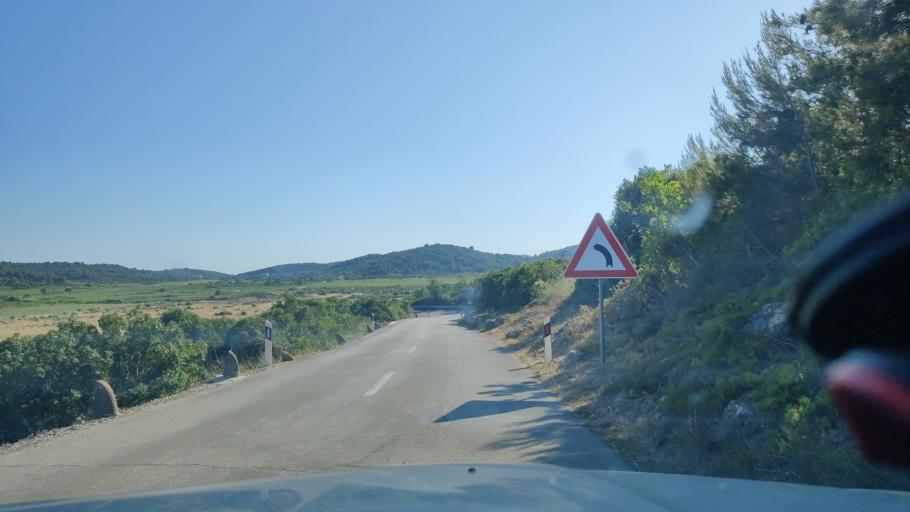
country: HR
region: Splitsko-Dalmatinska
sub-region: Grad Vis
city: Vis
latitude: 43.0432
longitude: 16.1968
